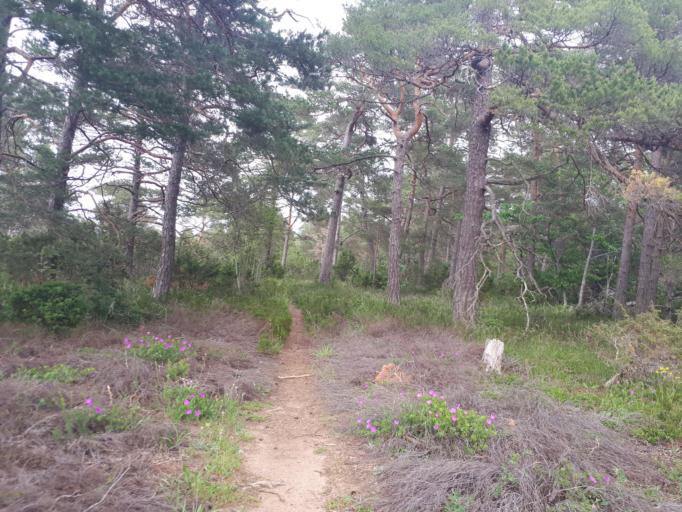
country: SE
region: Gotland
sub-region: Gotland
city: Visby
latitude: 57.6018
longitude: 18.3077
